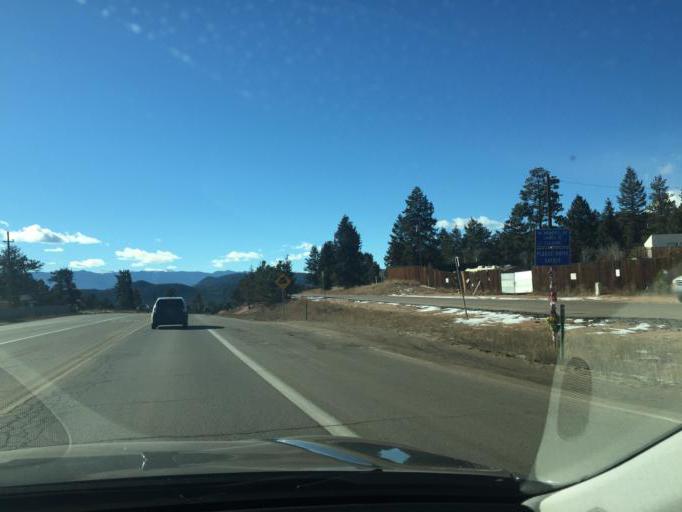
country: US
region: Colorado
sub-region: Jefferson County
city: Evergreen
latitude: 39.4909
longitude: -105.3480
